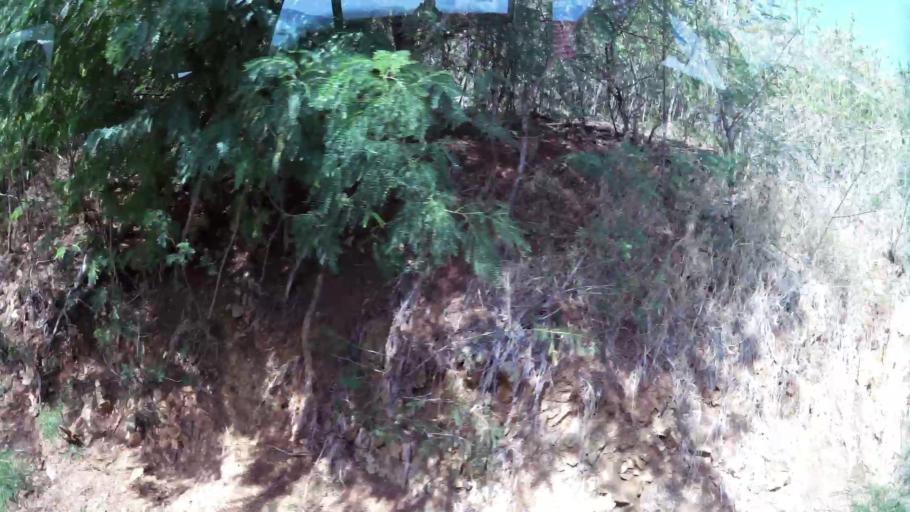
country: VG
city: Road Town
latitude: 18.4184
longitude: -64.6199
